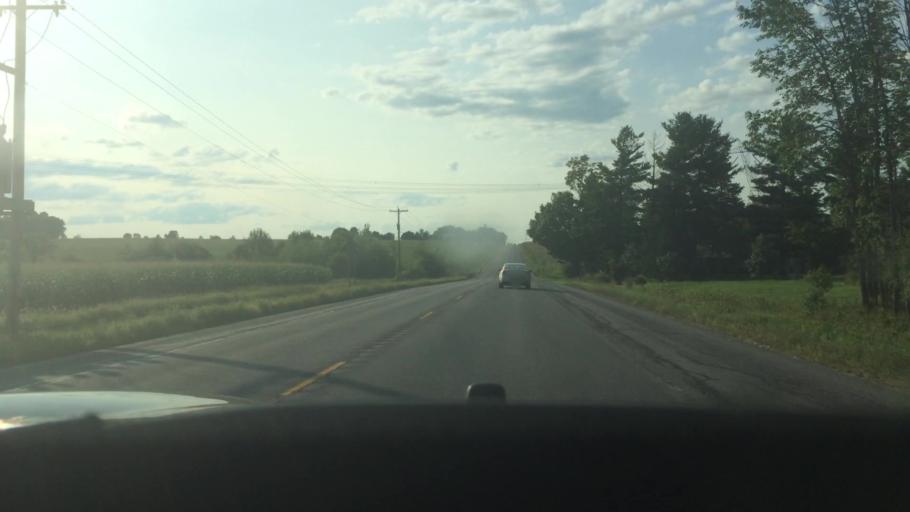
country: US
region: New York
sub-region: St. Lawrence County
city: Canton
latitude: 44.5977
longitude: -75.1913
